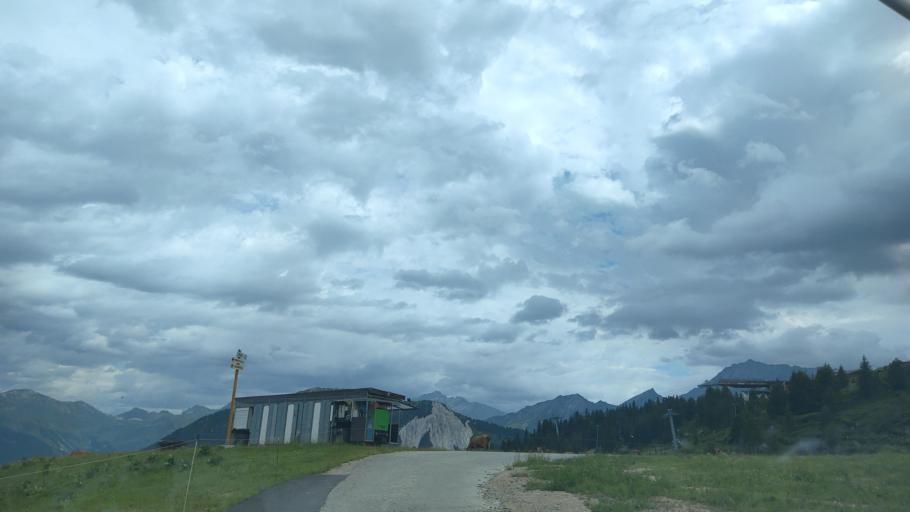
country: FR
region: Rhone-Alpes
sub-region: Departement de la Savoie
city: Courchevel
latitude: 45.3946
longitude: 6.6529
